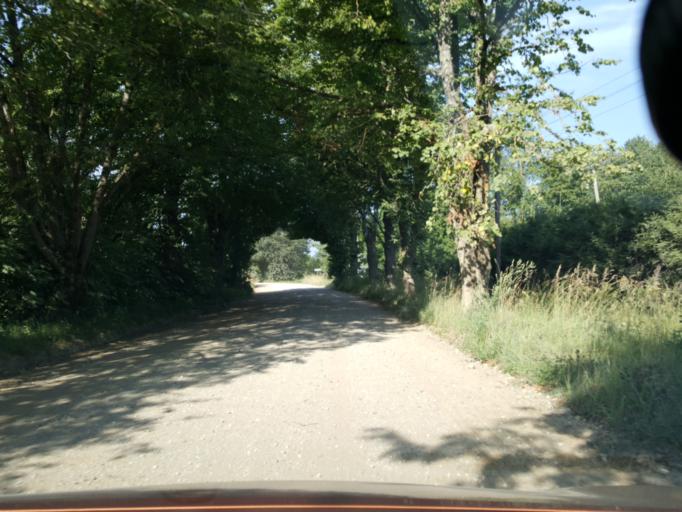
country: LV
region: Salacgrivas
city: Salacgriva
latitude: 57.7594
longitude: 24.4329
